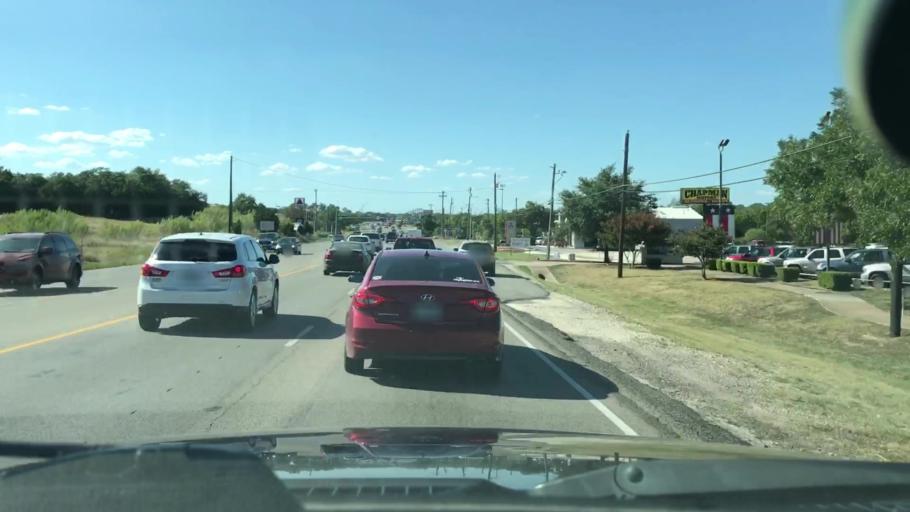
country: US
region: Texas
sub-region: Williamson County
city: Cedar Park
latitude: 30.4978
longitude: -97.8155
